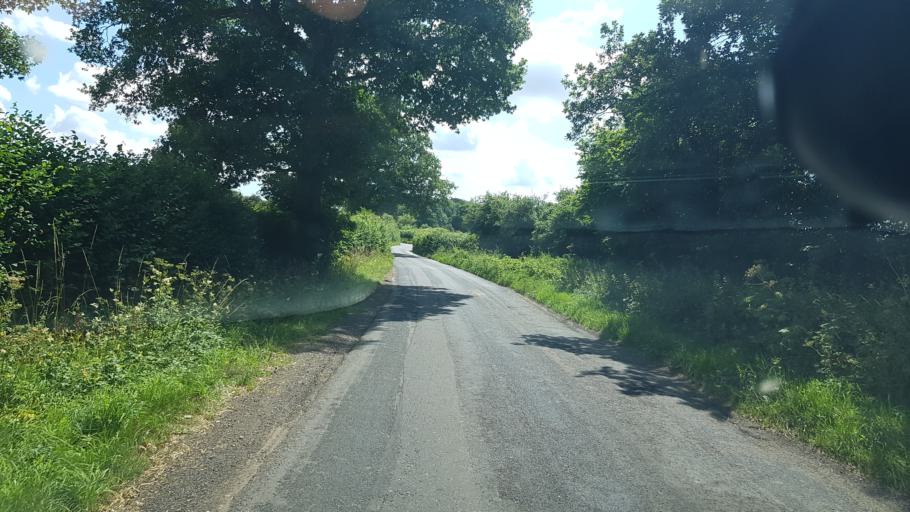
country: GB
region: England
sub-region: Kent
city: Edenbridge
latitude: 51.1971
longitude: 0.1358
